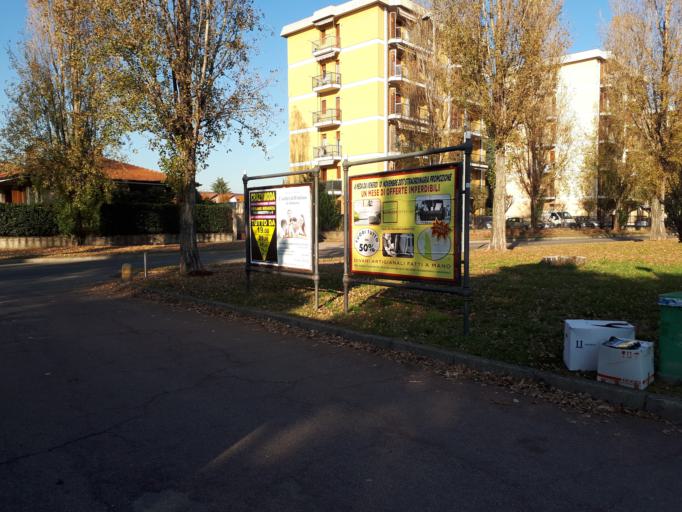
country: IT
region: Lombardy
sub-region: Provincia di Monza e Brianza
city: Carate Brianza
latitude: 45.6709
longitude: 9.2326
